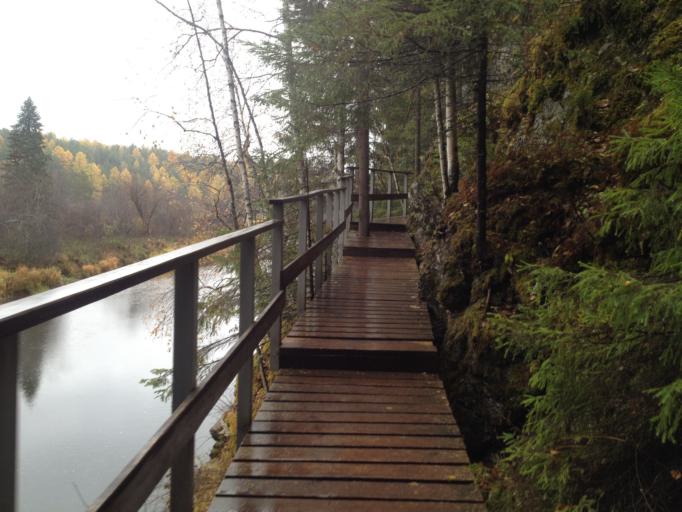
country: RU
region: Sverdlovsk
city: Mikhaylovsk
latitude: 56.5122
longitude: 59.2544
